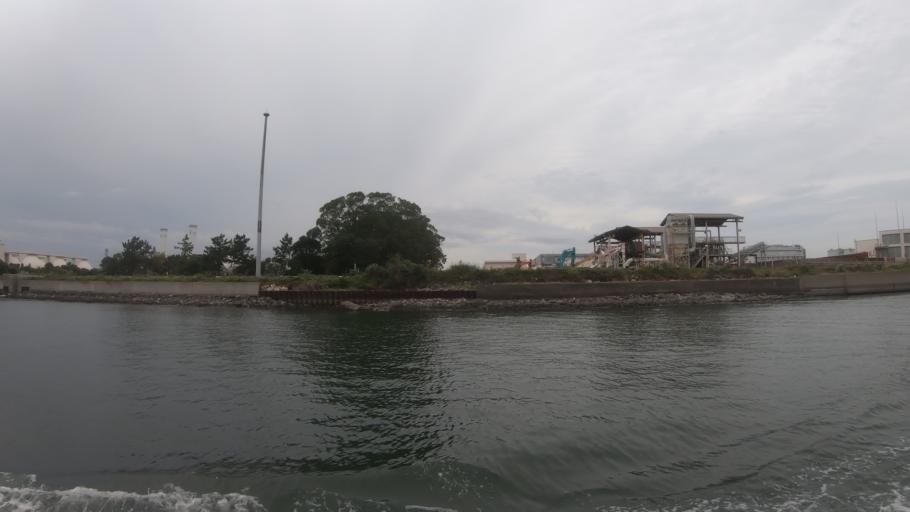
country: JP
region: Kanagawa
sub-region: Kawasaki-shi
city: Kawasaki
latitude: 35.4891
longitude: 139.6895
